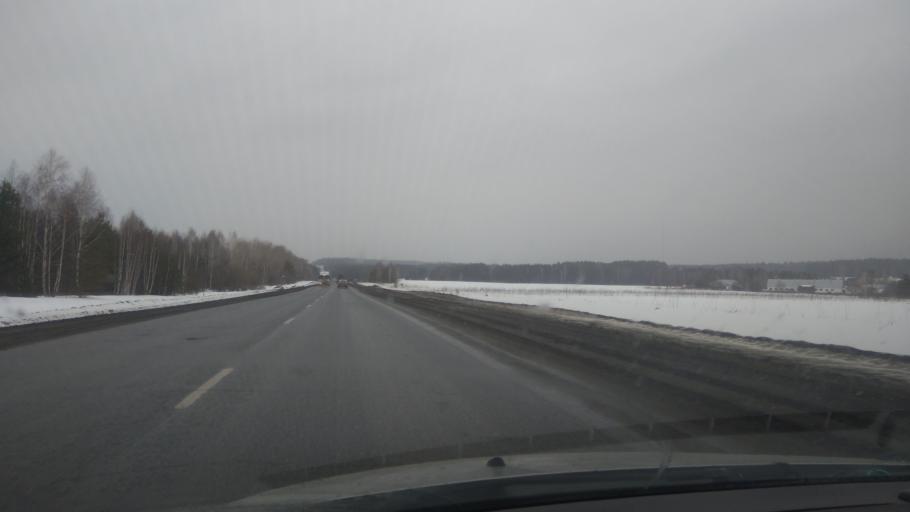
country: RU
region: Perm
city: Orda
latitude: 57.2959
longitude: 56.9885
